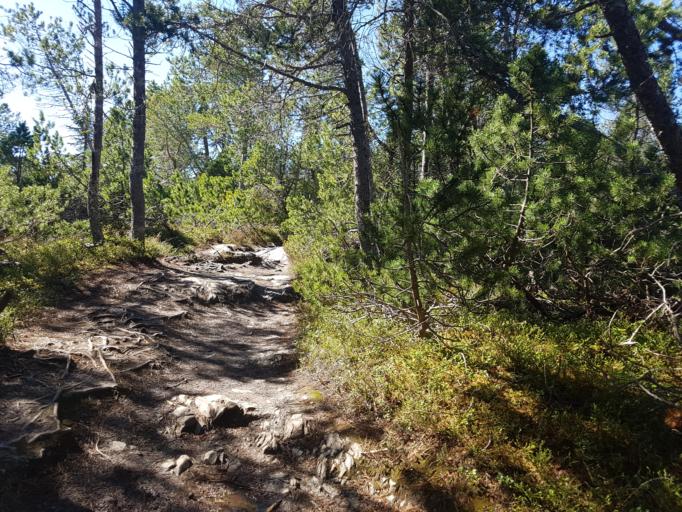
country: NO
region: Sor-Trondelag
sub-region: Trondheim
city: Trondheim
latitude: 63.4327
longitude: 10.3095
